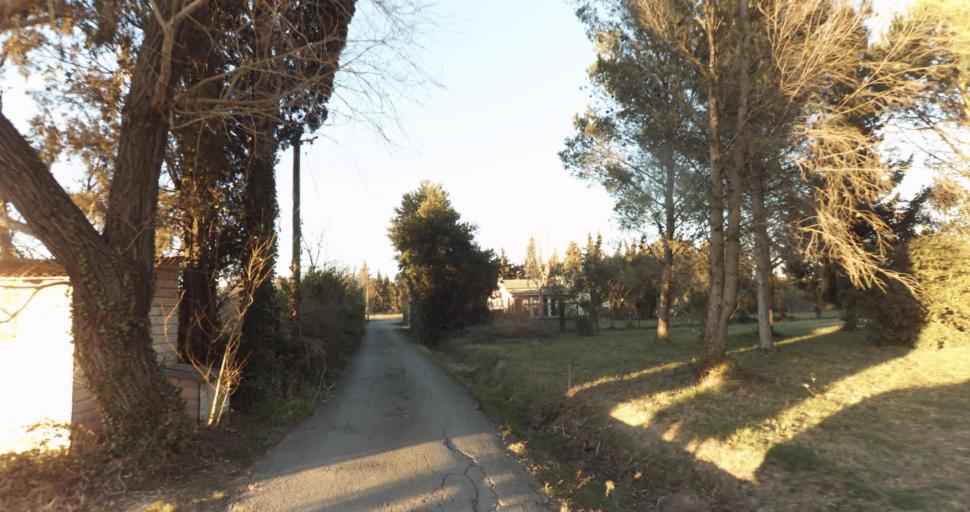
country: FR
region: Provence-Alpes-Cote d'Azur
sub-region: Departement des Bouches-du-Rhone
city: Barbentane
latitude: 43.8914
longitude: 4.7763
